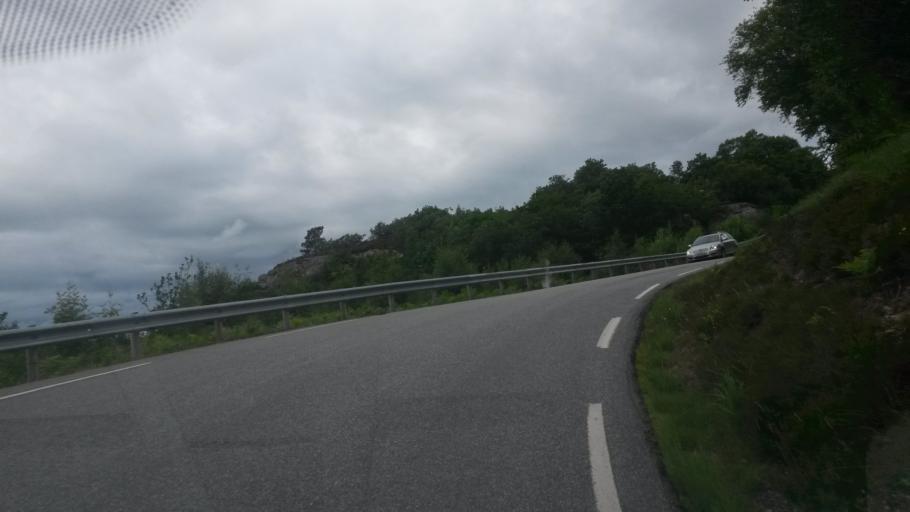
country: NO
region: Rogaland
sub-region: Sandnes
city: Sandnes
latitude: 58.8942
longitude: 5.7751
